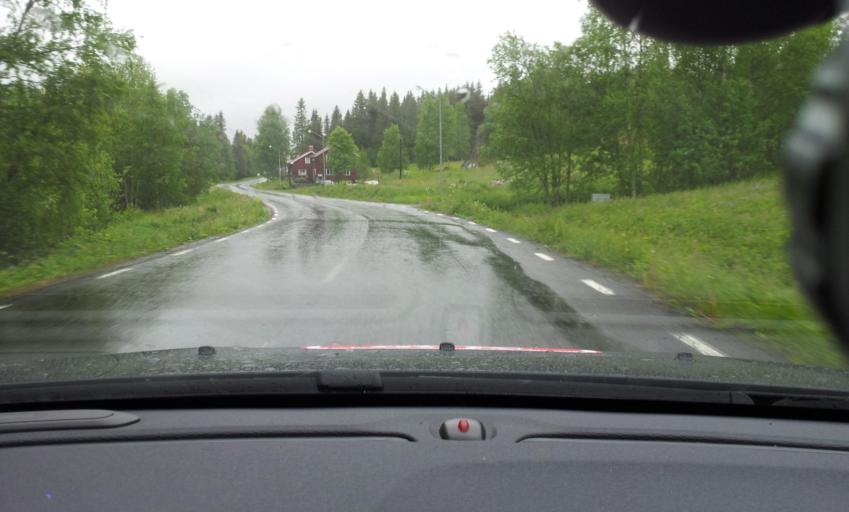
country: SE
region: Jaemtland
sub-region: Are Kommun
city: Are
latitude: 63.3158
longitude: 13.1088
